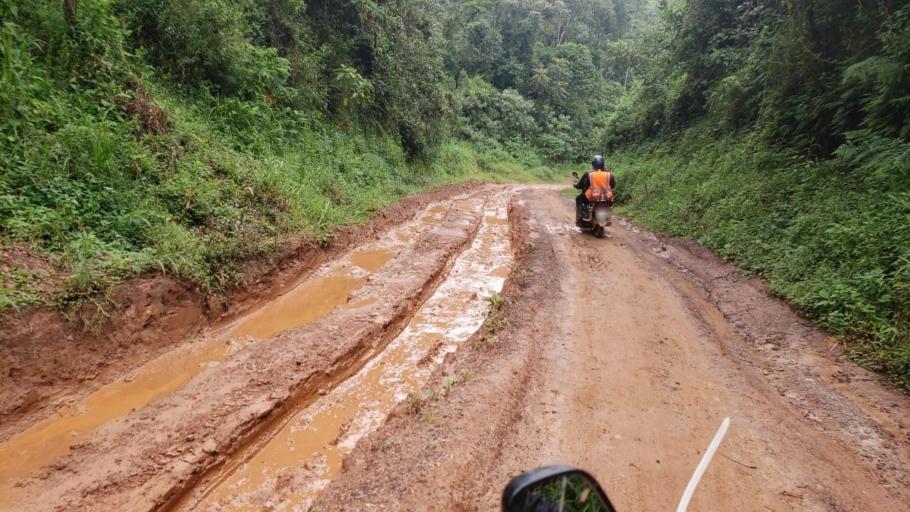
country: CD
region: South Kivu
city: Kabare
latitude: -2.2586
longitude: 28.6480
